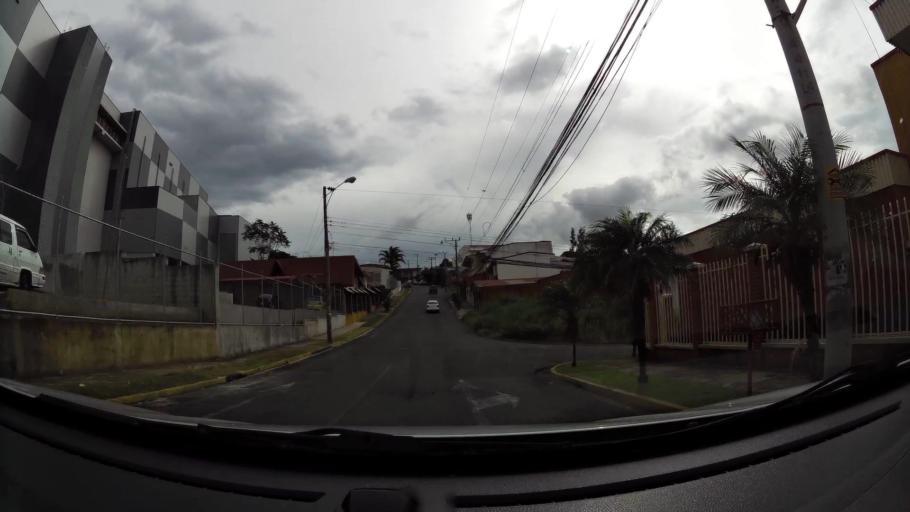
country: CR
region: San Jose
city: San Vicente de Moravia
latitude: 9.9614
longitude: -84.0566
